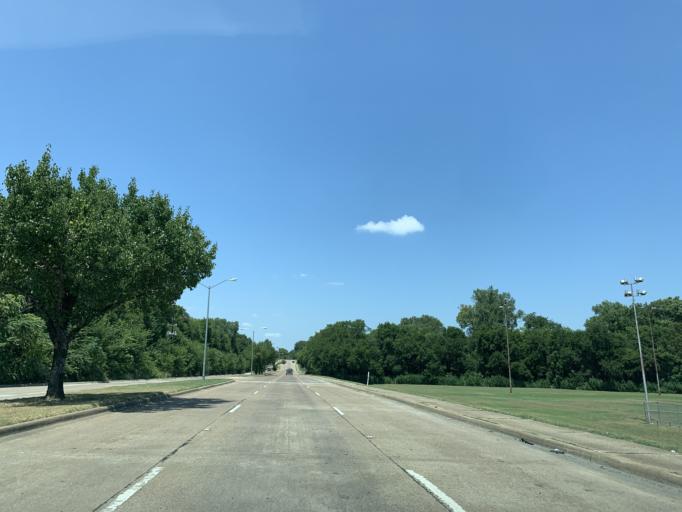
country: US
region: Texas
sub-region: Dallas County
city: Hutchins
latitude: 32.6850
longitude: -96.7686
